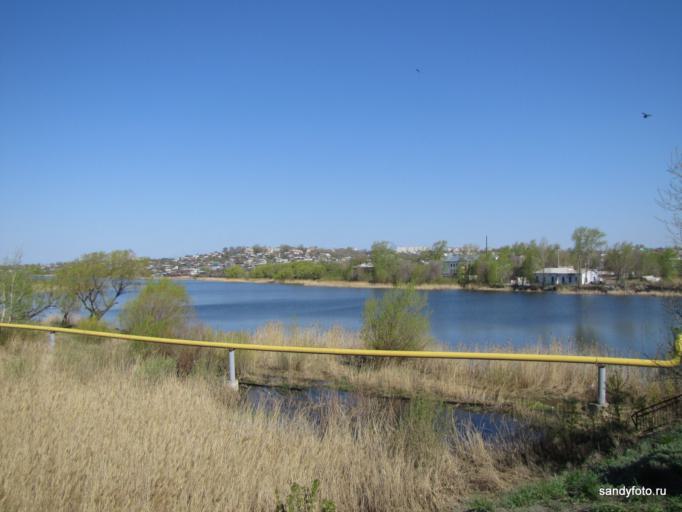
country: RU
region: Chelyabinsk
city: Troitsk
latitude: 54.0915
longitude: 61.5668
